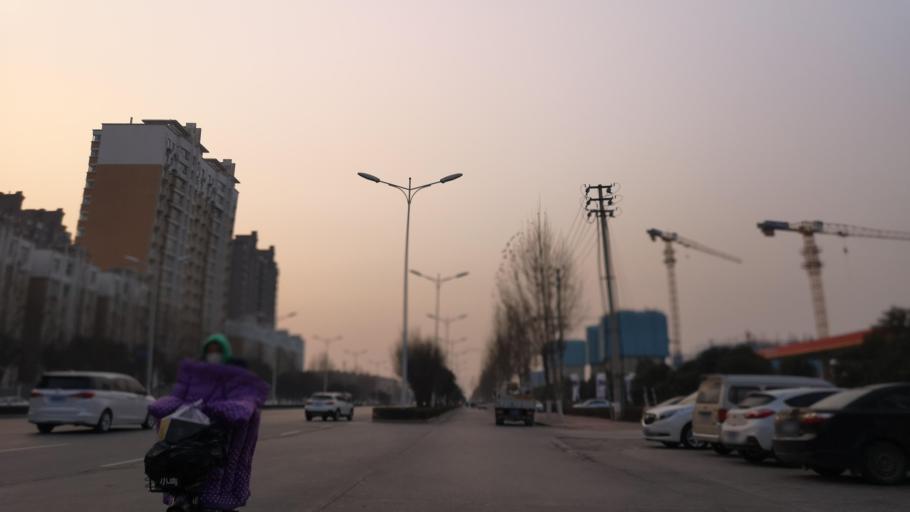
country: CN
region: Henan Sheng
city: Zhongyuanlu
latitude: 35.7894
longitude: 115.0858
